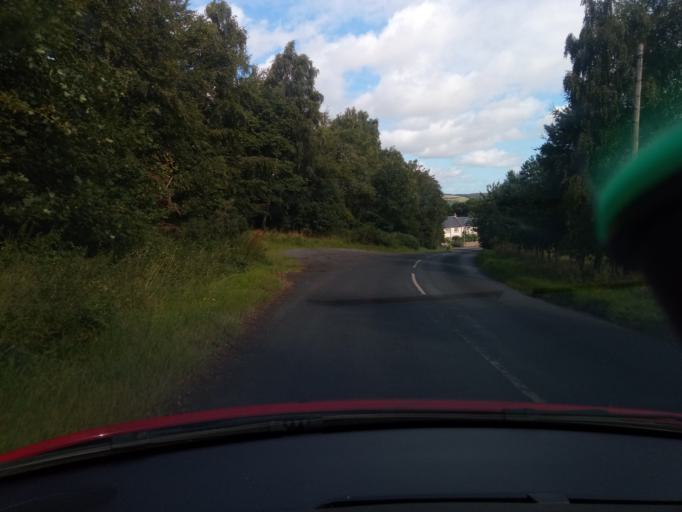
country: GB
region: Scotland
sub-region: The Scottish Borders
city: Melrose
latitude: 55.5838
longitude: -2.7351
